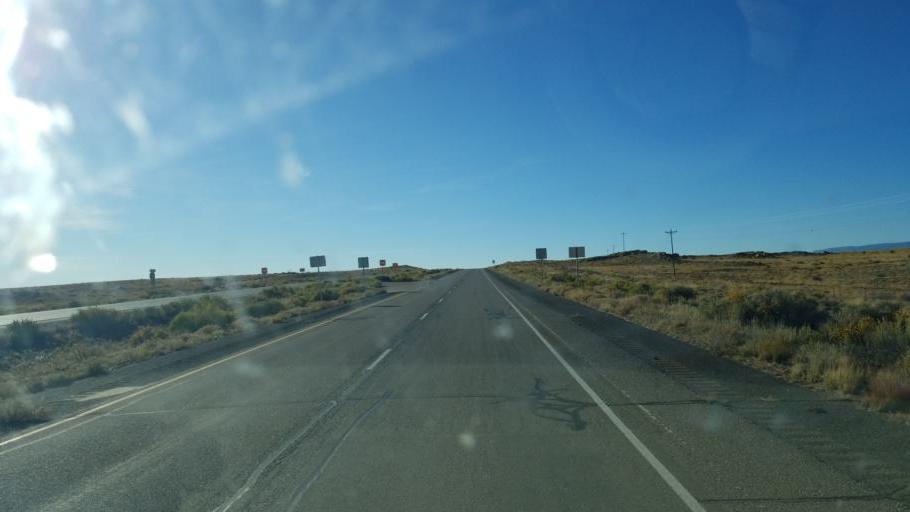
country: US
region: New Mexico
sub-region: San Juan County
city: Shiprock
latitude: 36.3550
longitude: -108.7189
